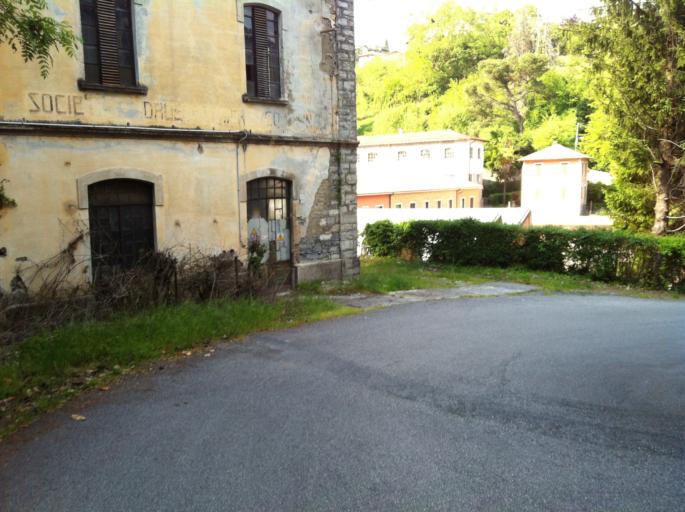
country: IT
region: Lombardy
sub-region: Provincia di Como
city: Menaggio
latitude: 46.0231
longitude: 9.2316
